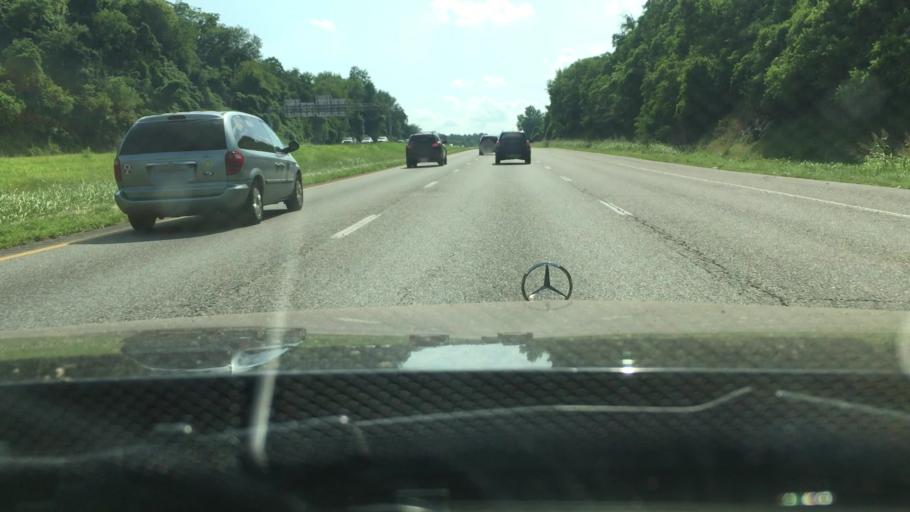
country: US
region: Virginia
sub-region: City of Charlottesville
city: Charlottesville
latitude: 38.0101
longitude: -78.4811
